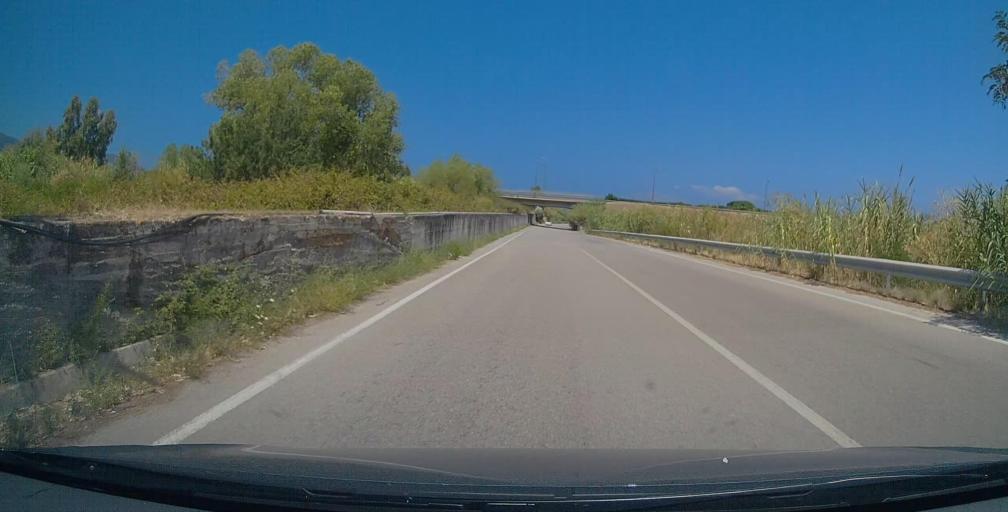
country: IT
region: Sicily
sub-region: Messina
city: Patti
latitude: 38.1415
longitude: 14.9965
